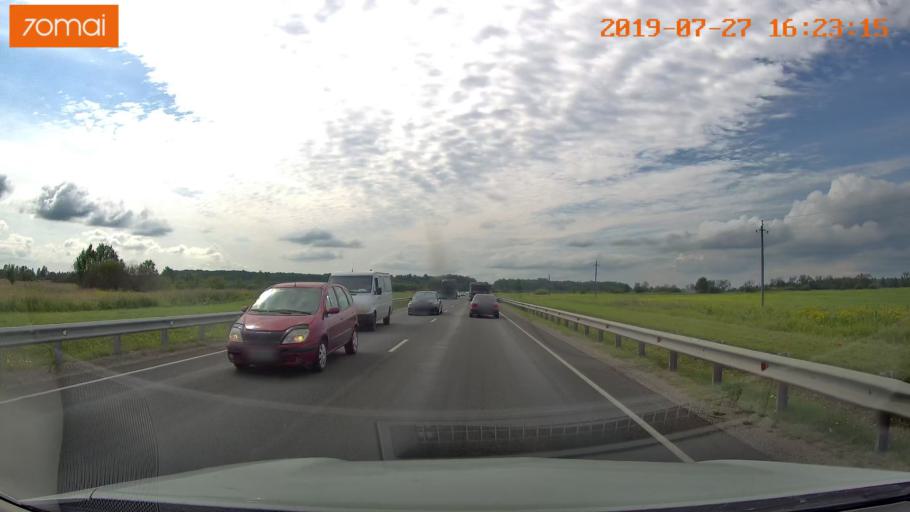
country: RU
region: Kaliningrad
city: Zheleznodorozhnyy
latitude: 54.6305
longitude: 21.4779
